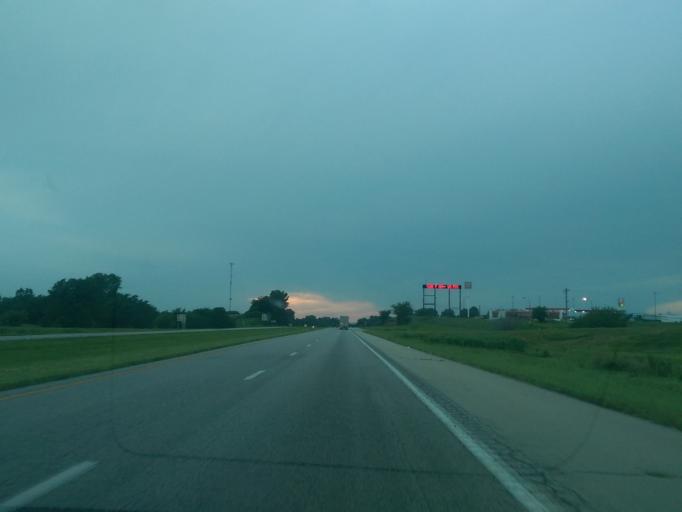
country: US
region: Missouri
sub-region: Holt County
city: Mound City
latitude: 40.0749
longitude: -95.1935
